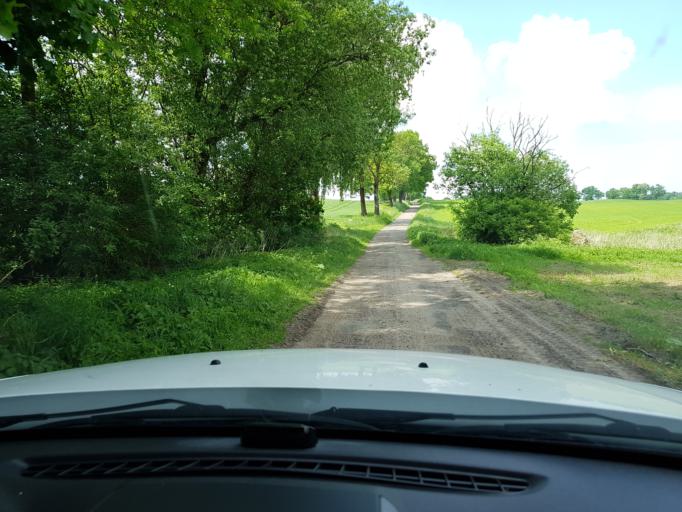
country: PL
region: West Pomeranian Voivodeship
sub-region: Powiat drawski
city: Drawsko Pomorskie
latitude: 53.5273
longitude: 15.7477
